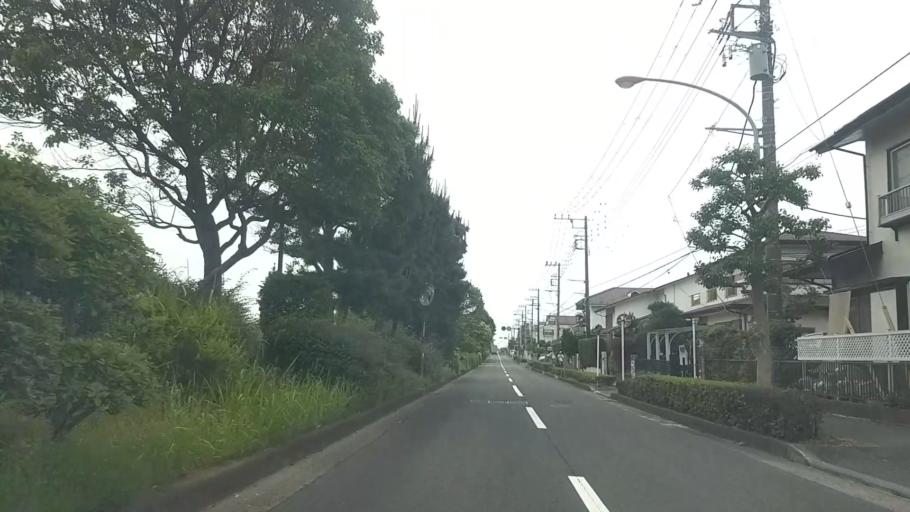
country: JP
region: Kanagawa
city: Fujisawa
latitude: 35.3279
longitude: 139.4635
